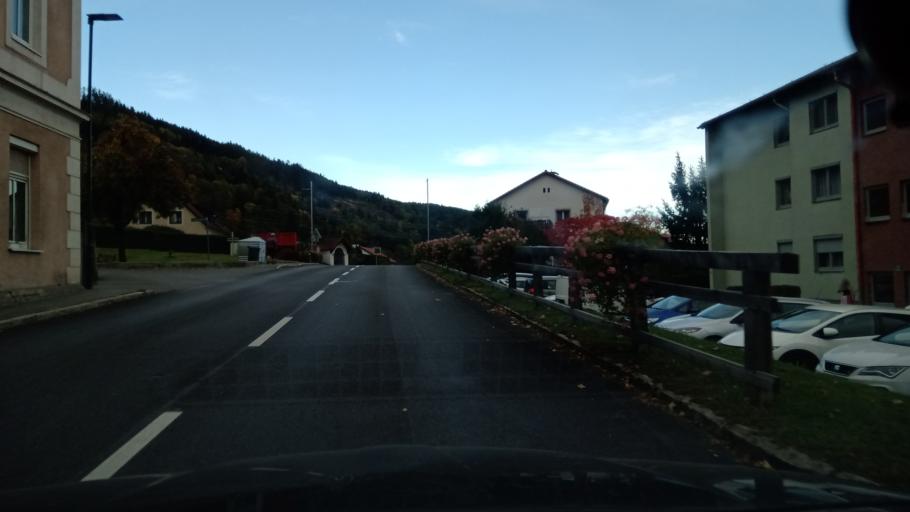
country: AT
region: Styria
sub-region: Politischer Bezirk Leoben
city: Proleb
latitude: 47.3965
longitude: 15.1349
